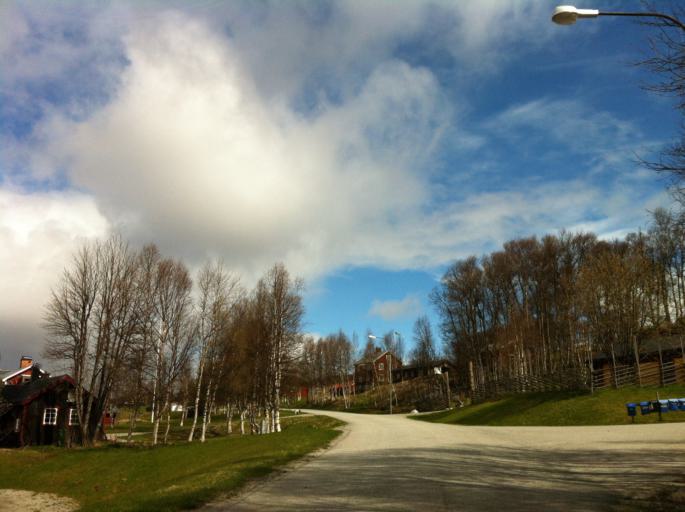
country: NO
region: Sor-Trondelag
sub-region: Tydal
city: Aas
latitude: 62.6300
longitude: 12.4469
